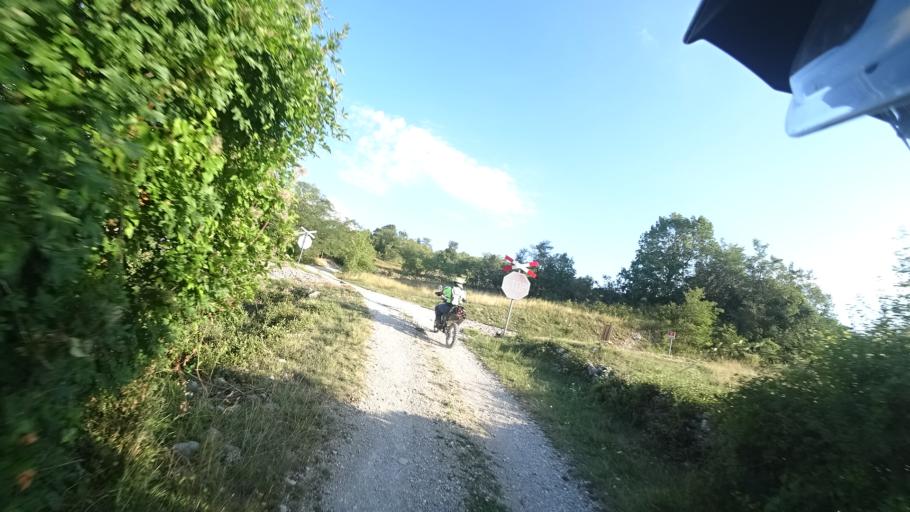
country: HR
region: Sibensko-Kniniska
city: Knin
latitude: 44.1592
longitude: 16.0932
